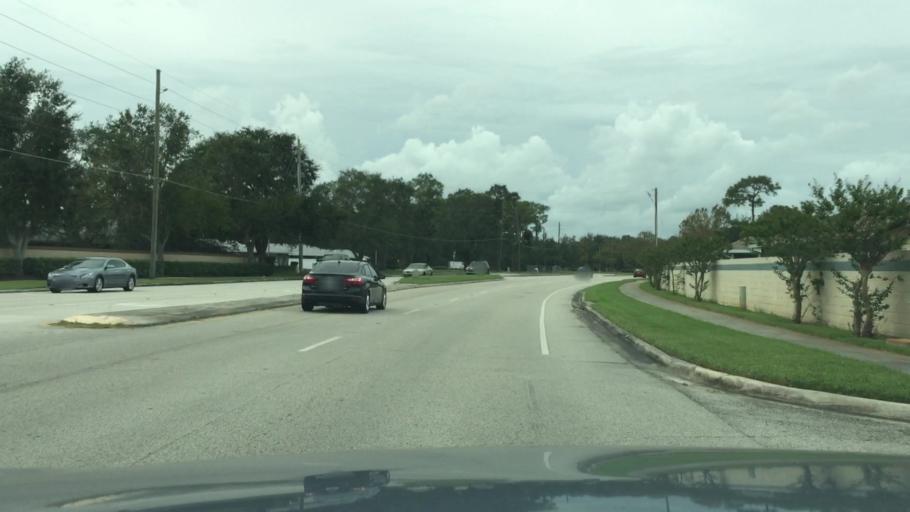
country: US
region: Florida
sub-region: Osceola County
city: Saint Cloud
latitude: 28.2282
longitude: -81.3117
